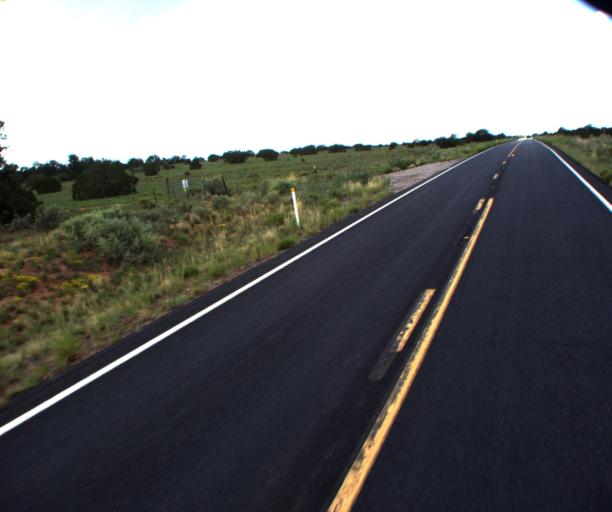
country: US
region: Arizona
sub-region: Coconino County
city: Parks
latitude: 35.6067
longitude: -112.0489
